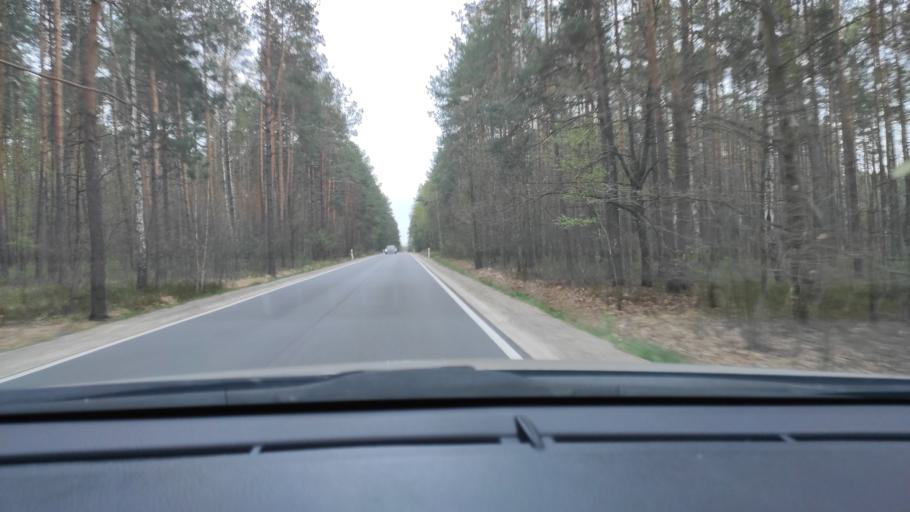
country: PL
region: Masovian Voivodeship
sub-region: Powiat zwolenski
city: Zwolen
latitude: 51.3920
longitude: 21.5475
